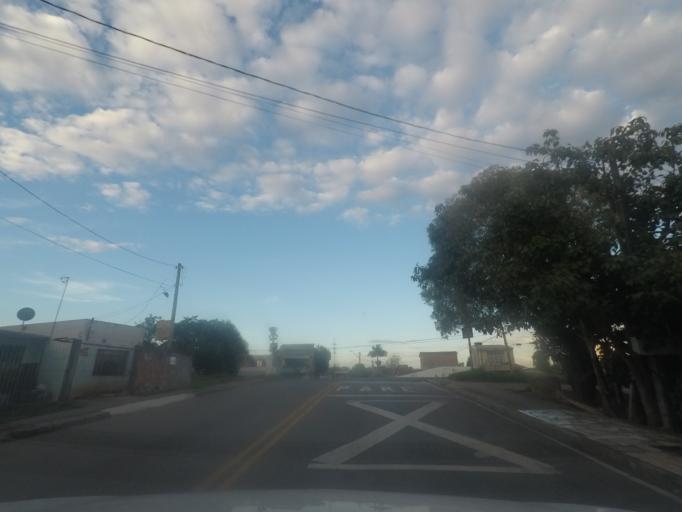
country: BR
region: Parana
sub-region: Pinhais
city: Pinhais
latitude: -25.4651
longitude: -49.1984
